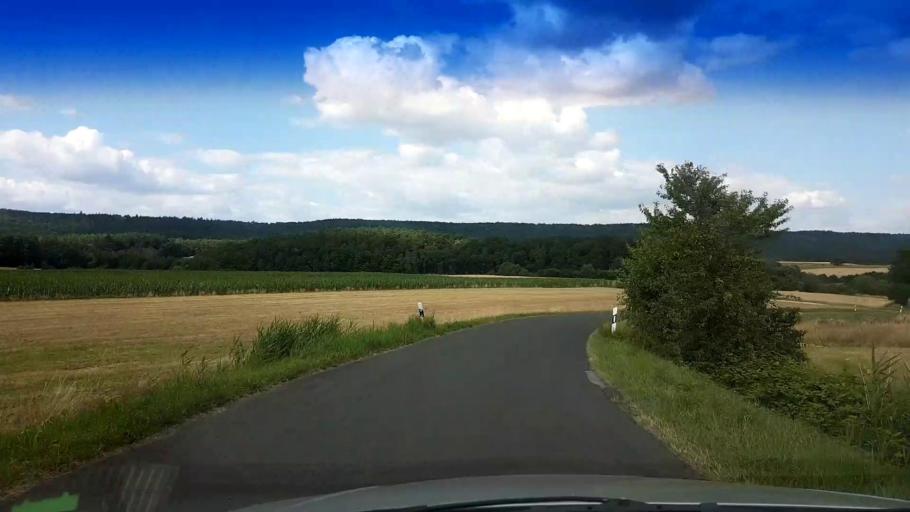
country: DE
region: Bavaria
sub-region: Upper Franconia
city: Lauter
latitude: 49.9989
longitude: 10.7699
